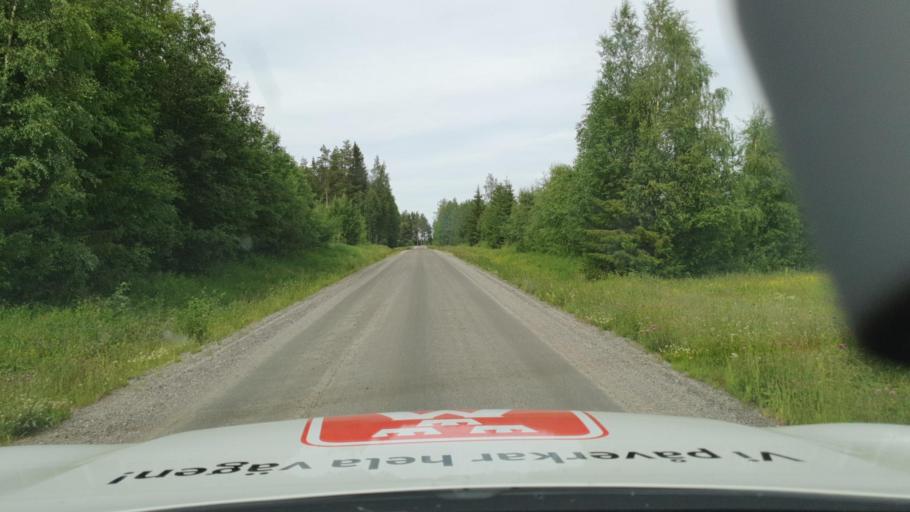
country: SE
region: Vaesterbotten
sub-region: Skelleftea Kommun
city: Viken
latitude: 64.5052
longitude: 20.9289
